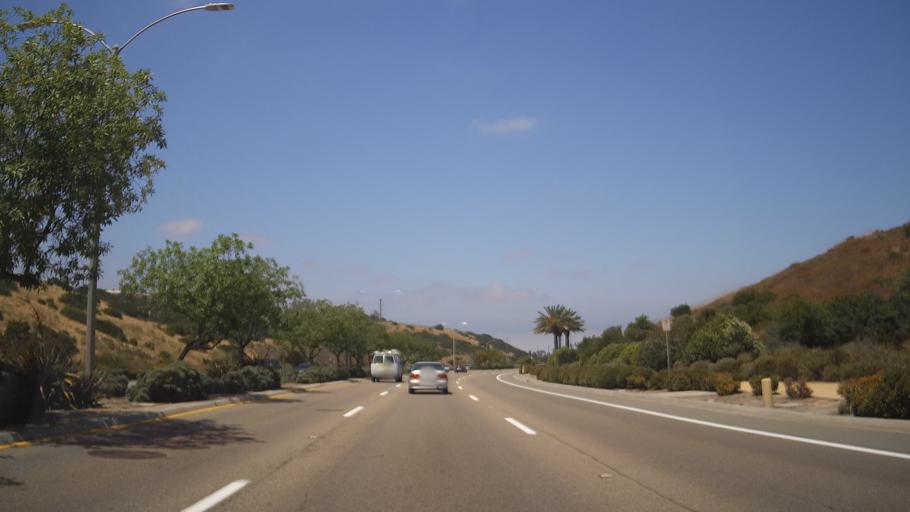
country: US
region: California
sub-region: San Diego County
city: Bonita
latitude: 32.6096
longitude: -117.0174
